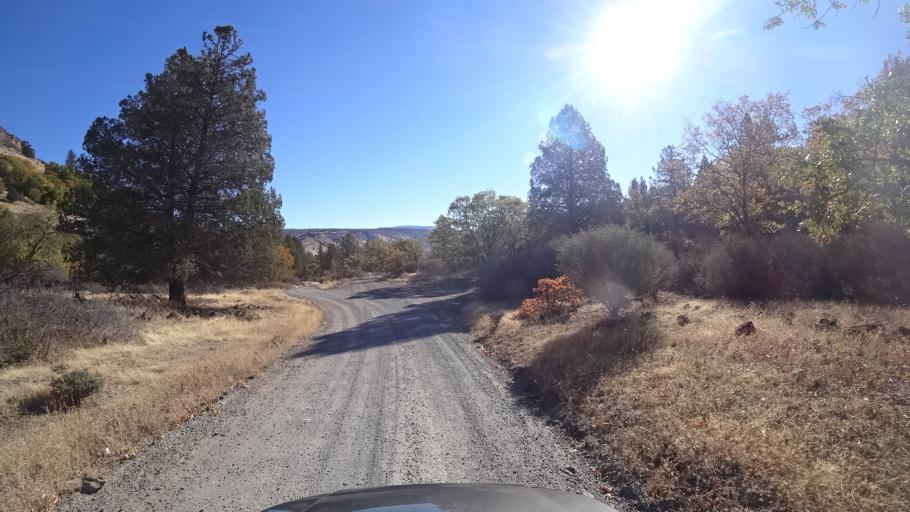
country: US
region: California
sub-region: Siskiyou County
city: Montague
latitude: 41.9855
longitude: -122.3345
